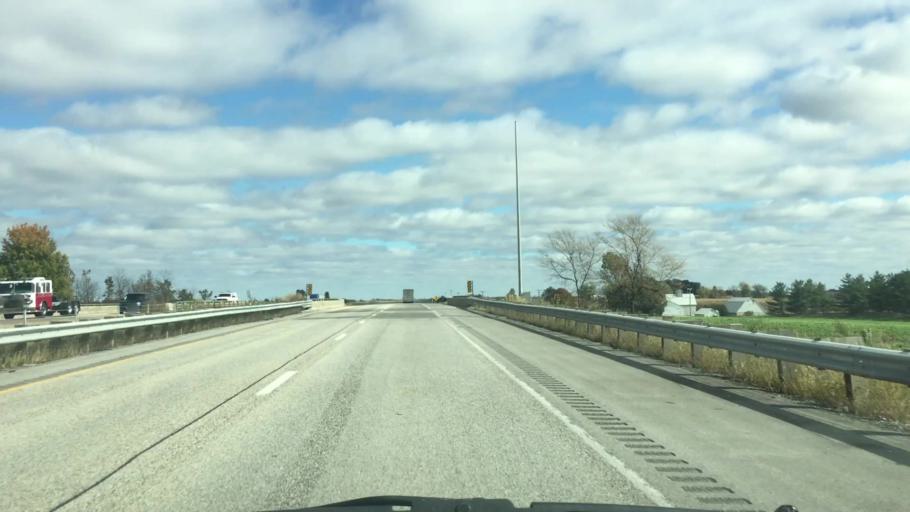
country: US
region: Iowa
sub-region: Iowa County
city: Marengo
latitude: 41.6959
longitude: -92.1634
